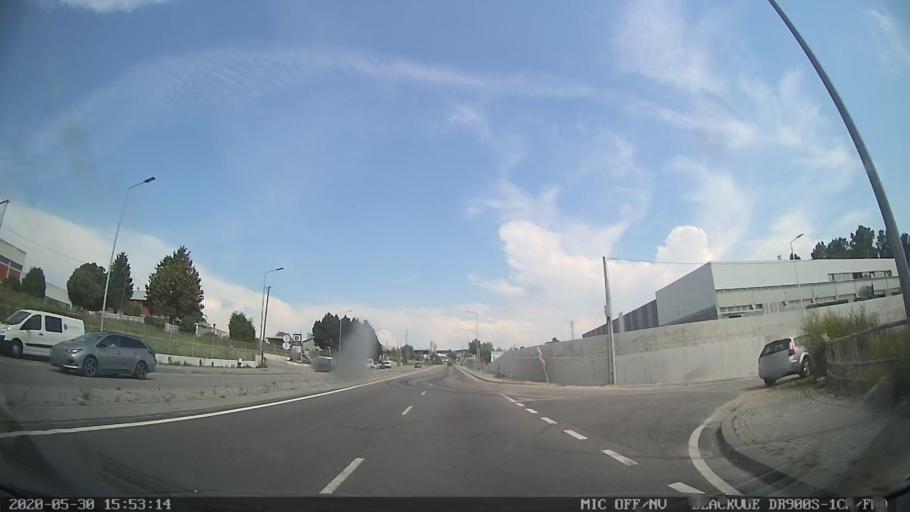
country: PT
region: Porto
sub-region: Paredes
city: Paredes
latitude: 41.1991
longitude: -8.3117
